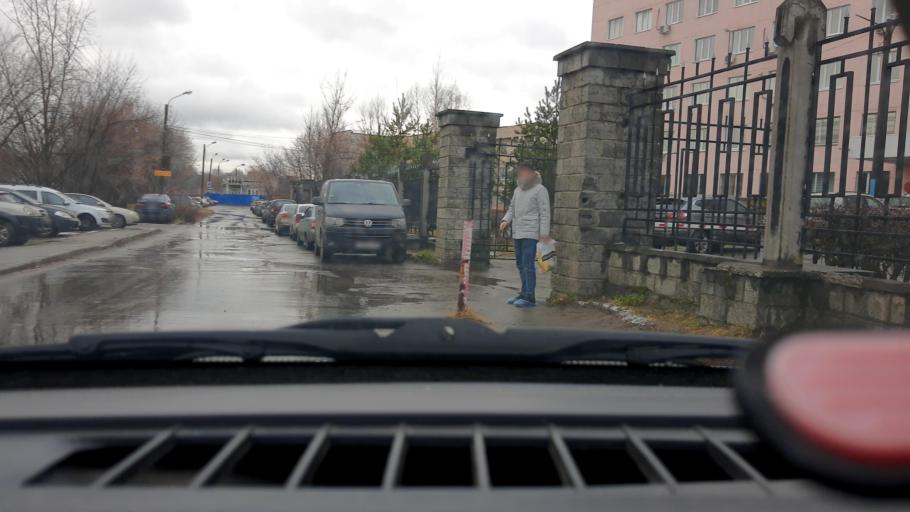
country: RU
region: Nizjnij Novgorod
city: Nizhniy Novgorod
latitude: 56.2947
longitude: 43.9292
